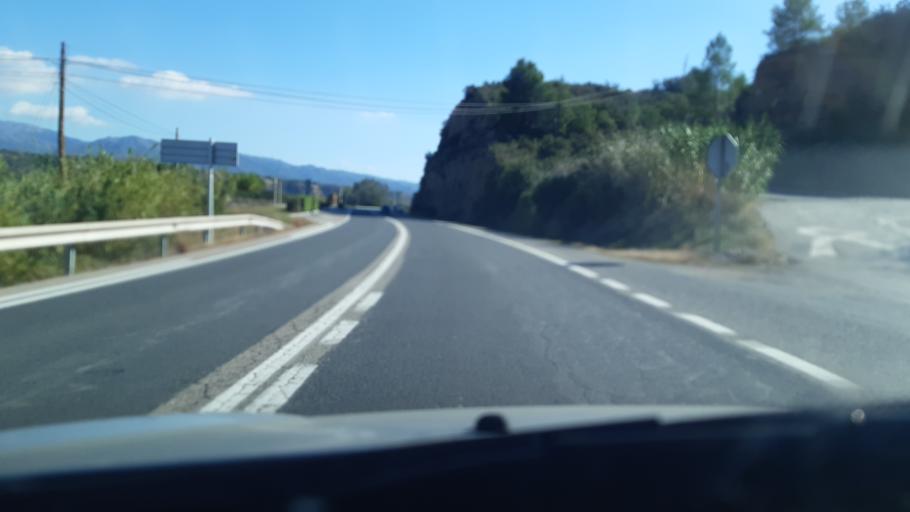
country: ES
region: Catalonia
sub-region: Provincia de Tarragona
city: Tivenys
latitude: 40.8982
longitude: 0.4855
